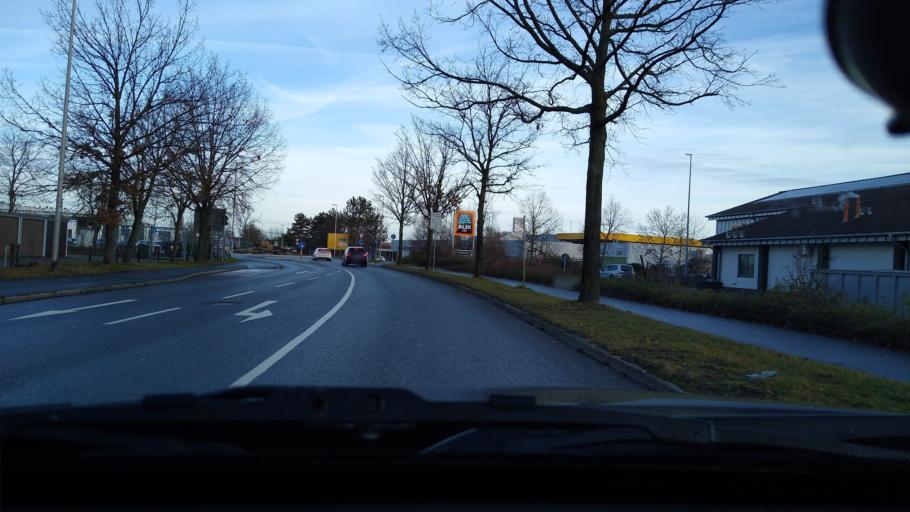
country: DE
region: Bavaria
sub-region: Regierungsbezirk Mittelfranken
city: Herzogenaurach
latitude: 49.5781
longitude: 10.8836
